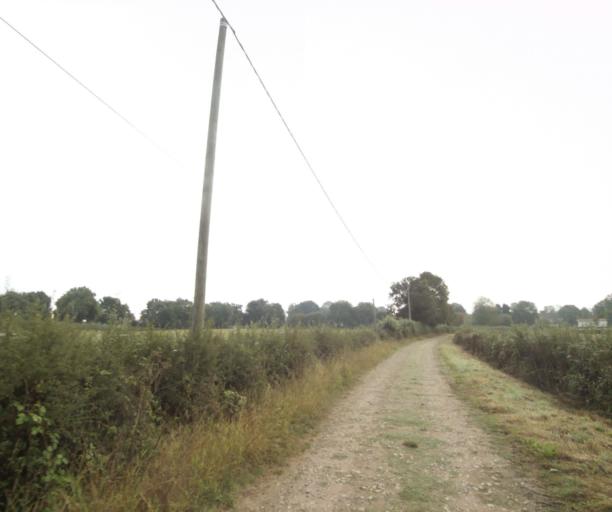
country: FR
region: Bourgogne
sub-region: Departement de Saone-et-Loire
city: Charolles
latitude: 46.4343
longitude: 4.2937
